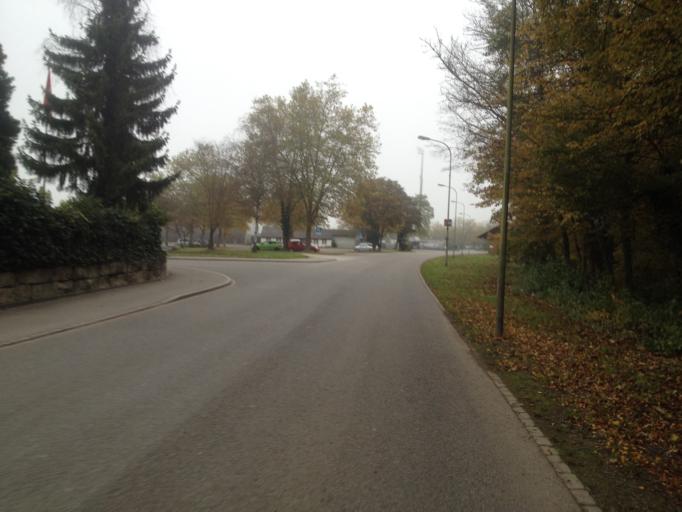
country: CH
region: Aargau
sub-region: Bezirk Brugg
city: Windisch
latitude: 47.4883
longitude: 8.2195
